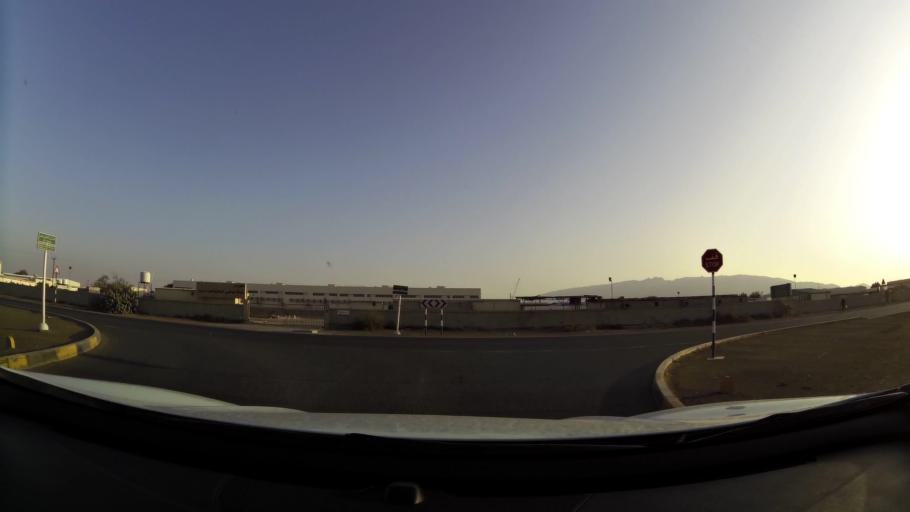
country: AE
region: Abu Dhabi
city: Al Ain
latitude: 24.1505
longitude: 55.8245
